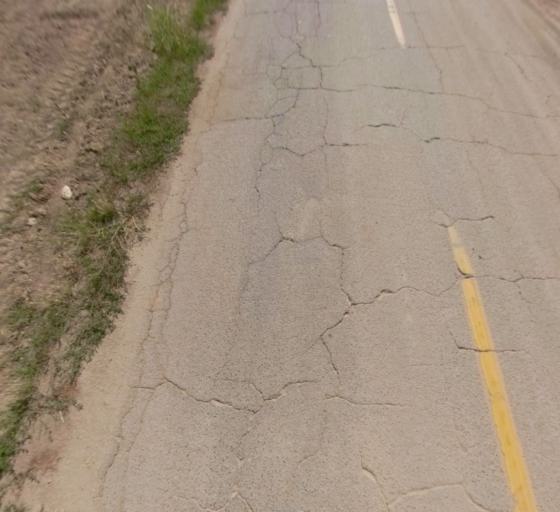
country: US
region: California
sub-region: Fresno County
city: Biola
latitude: 36.8658
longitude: -119.9510
